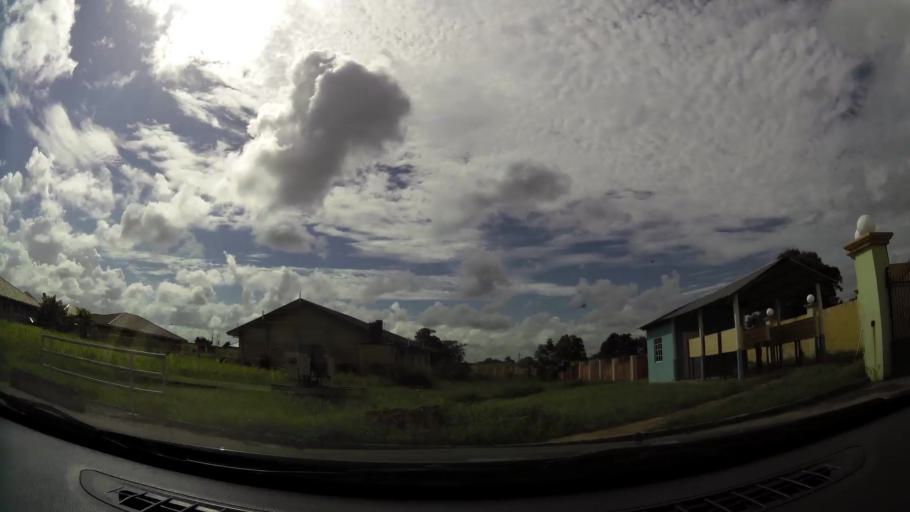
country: TT
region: Chaguanas
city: Chaguanas
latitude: 10.5076
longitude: -61.3855
